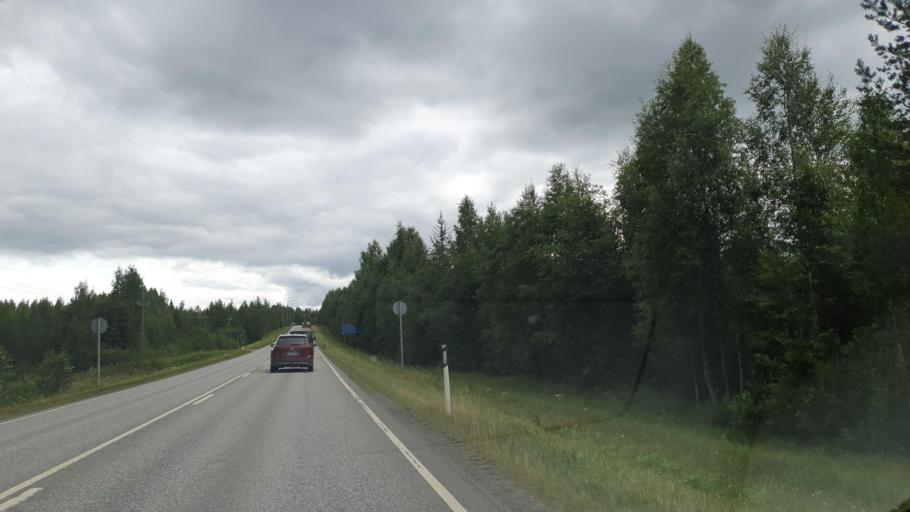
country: FI
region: Northern Savo
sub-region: Ylae-Savo
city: Sonkajaervi
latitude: 63.7027
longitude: 27.3568
